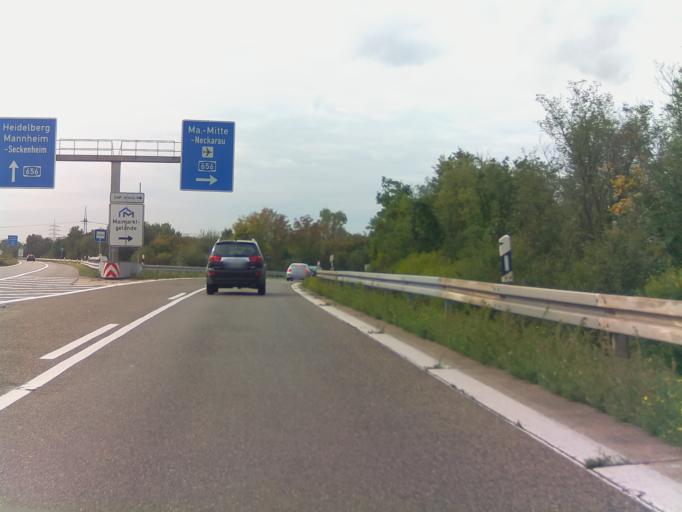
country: DE
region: Baden-Wuerttemberg
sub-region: Karlsruhe Region
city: Ilvesheim
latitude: 49.4646
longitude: 8.5395
